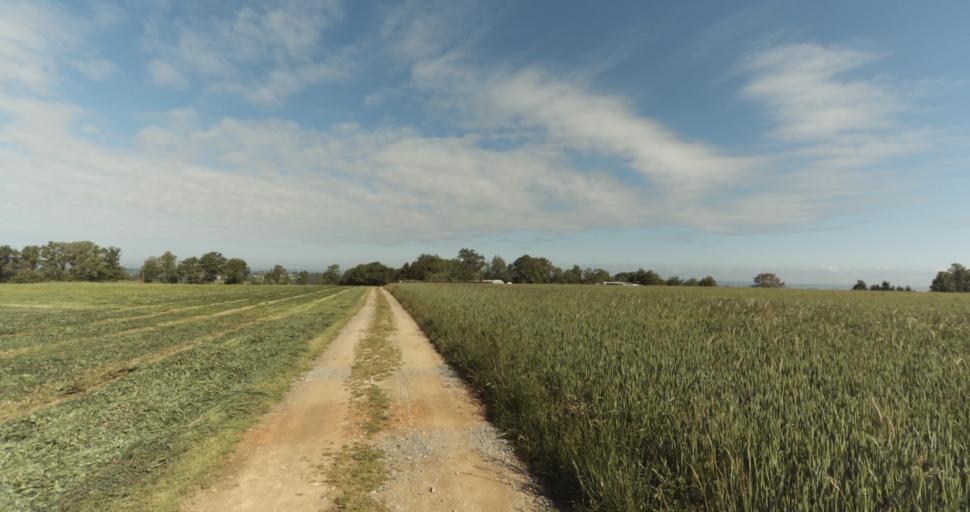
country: FR
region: Limousin
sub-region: Departement de la Haute-Vienne
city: Solignac
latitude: 45.7231
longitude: 1.2426
